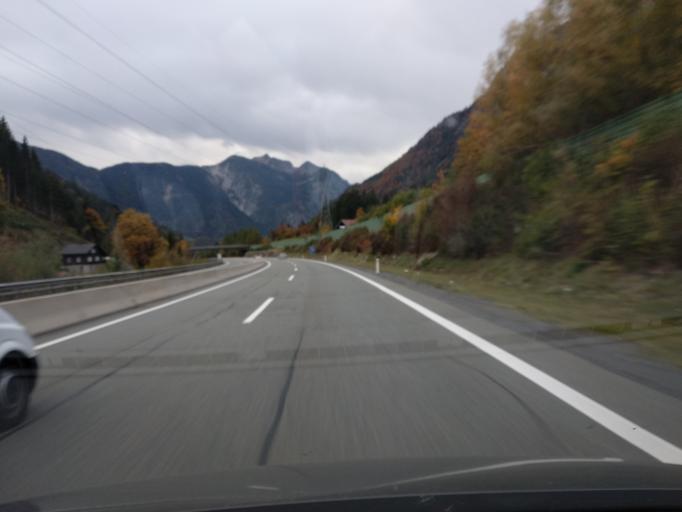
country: AT
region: Vorarlberg
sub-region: Politischer Bezirk Bludenz
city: Dalaas
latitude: 47.1281
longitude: 10.0326
